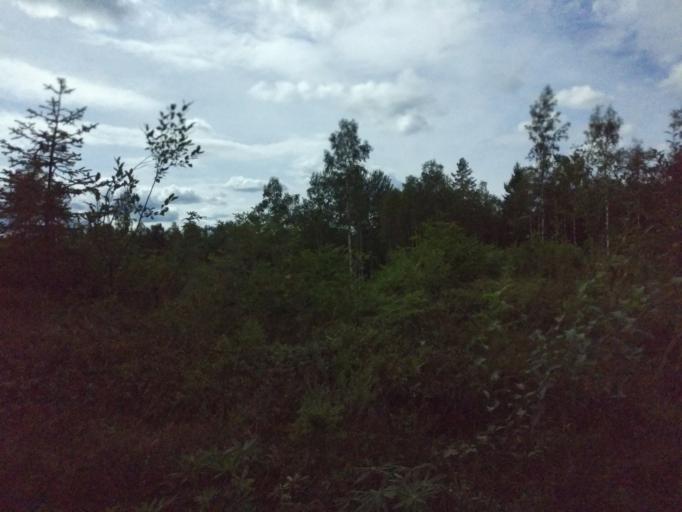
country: SE
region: Vaermland
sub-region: Hagfors Kommun
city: Hagfors
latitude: 60.0101
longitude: 13.6944
